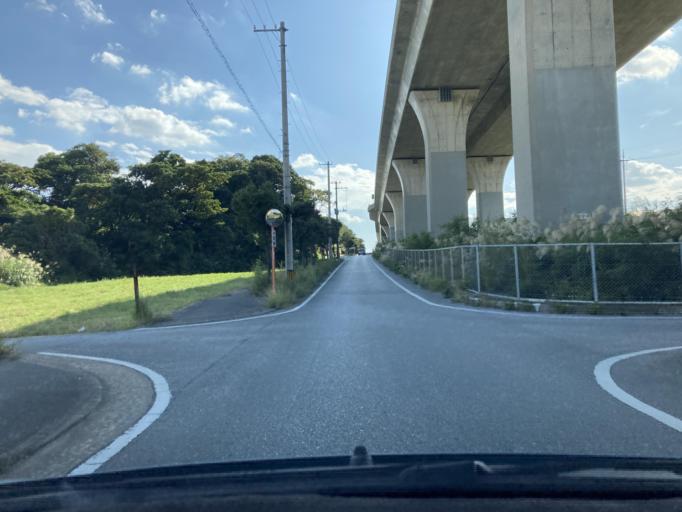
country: JP
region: Okinawa
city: Tomigusuku
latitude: 26.1919
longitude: 127.7392
